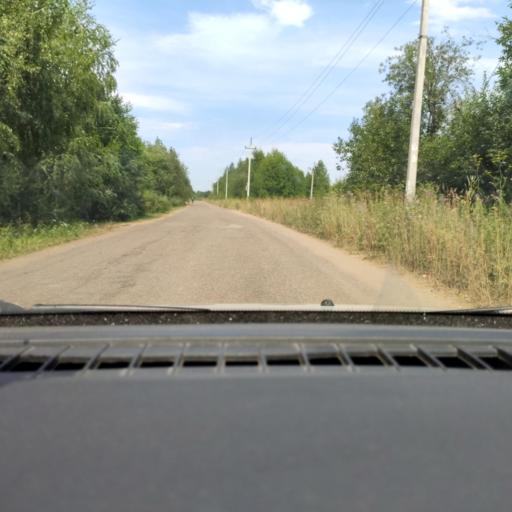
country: RU
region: Perm
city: Polazna
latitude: 58.1794
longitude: 56.4219
